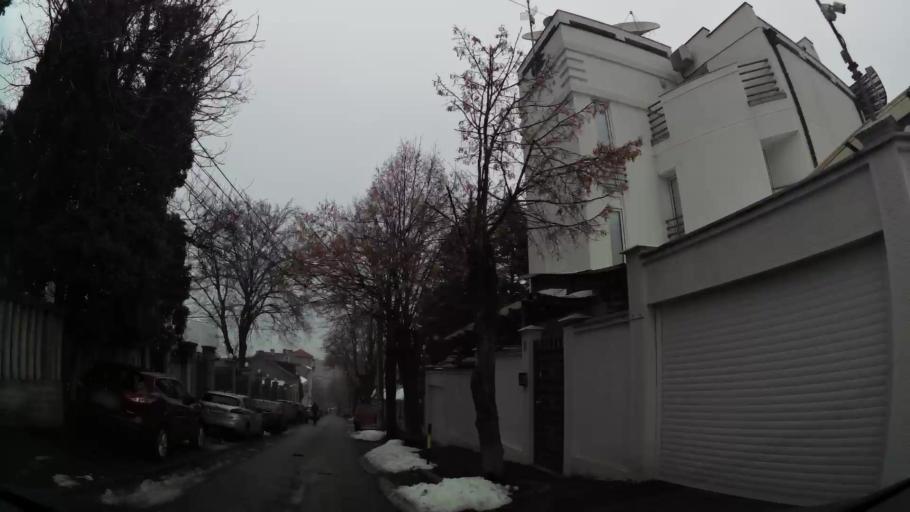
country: RS
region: Central Serbia
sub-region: Belgrade
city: Savski Venac
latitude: 44.7930
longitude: 20.4413
